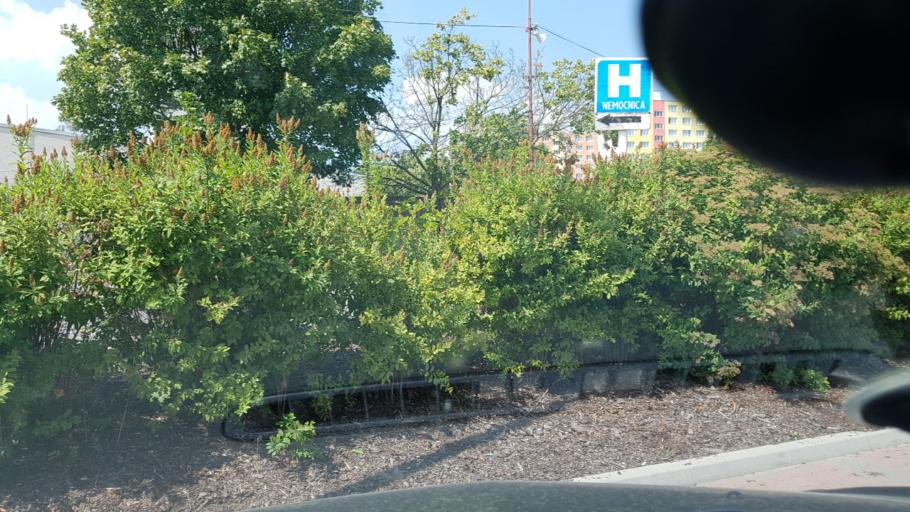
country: SK
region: Banskobystricky
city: Velky Krtis
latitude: 48.2110
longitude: 19.3523
